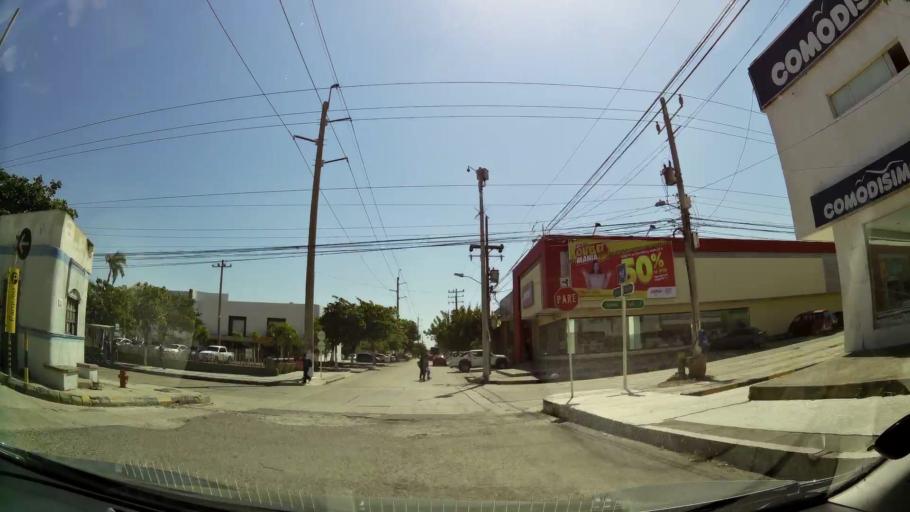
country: CO
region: Atlantico
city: Barranquilla
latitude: 11.0127
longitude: -74.7981
